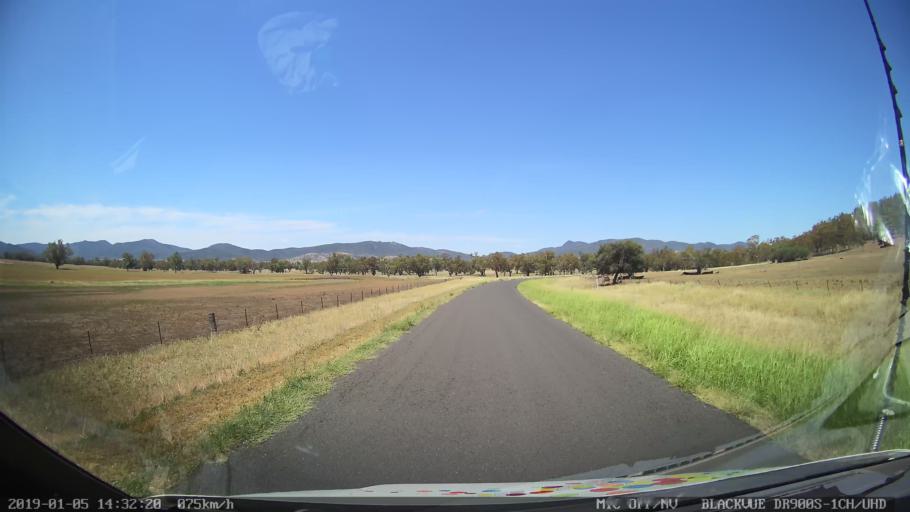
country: AU
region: New South Wales
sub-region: Tamworth Municipality
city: Phillip
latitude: -31.2211
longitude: 150.6169
